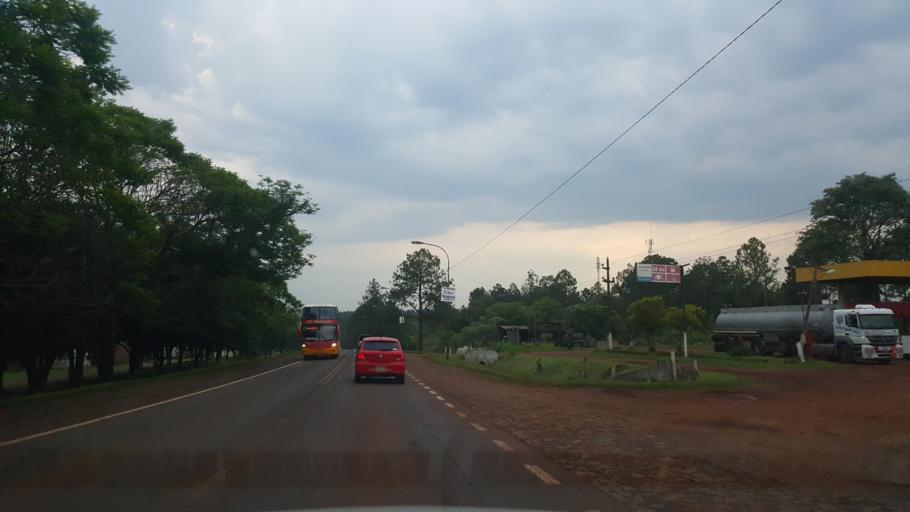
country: AR
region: Misiones
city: Santo Pipo
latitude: -27.1447
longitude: -55.4081
